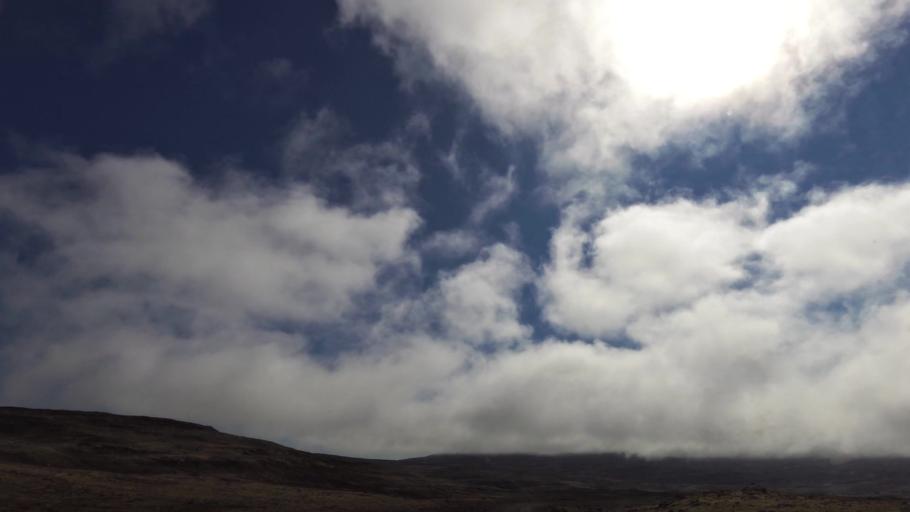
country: IS
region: West
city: Olafsvik
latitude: 65.5533
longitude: -24.2617
